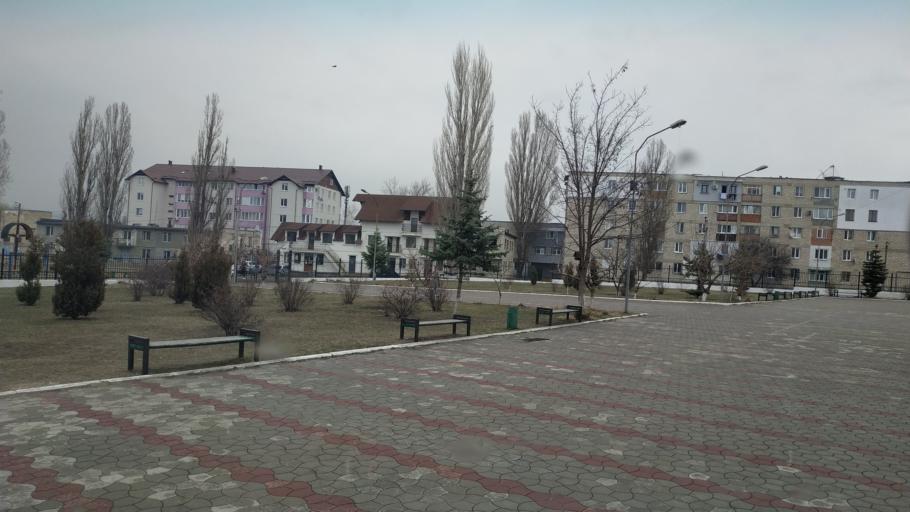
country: MD
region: Chisinau
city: Singera
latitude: 46.9145
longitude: 28.9738
